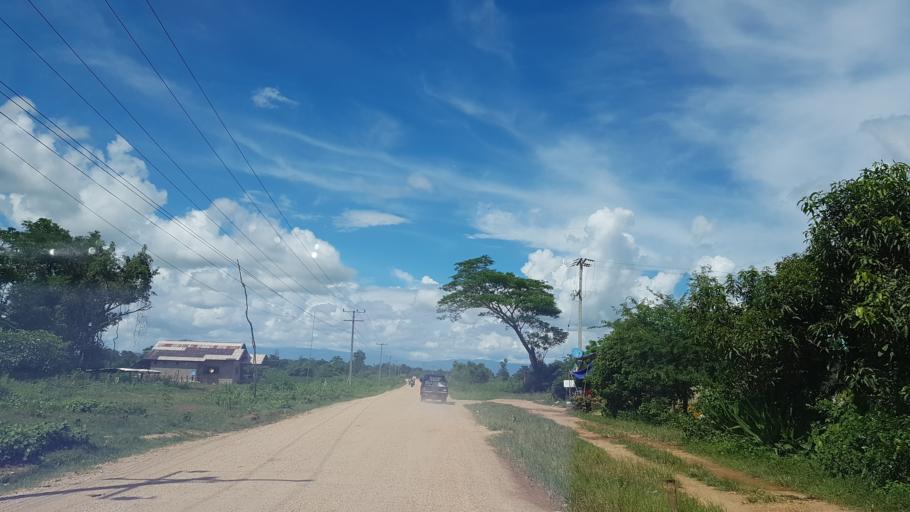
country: LA
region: Vientiane
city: Vientiane
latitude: 18.2317
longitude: 102.5267
